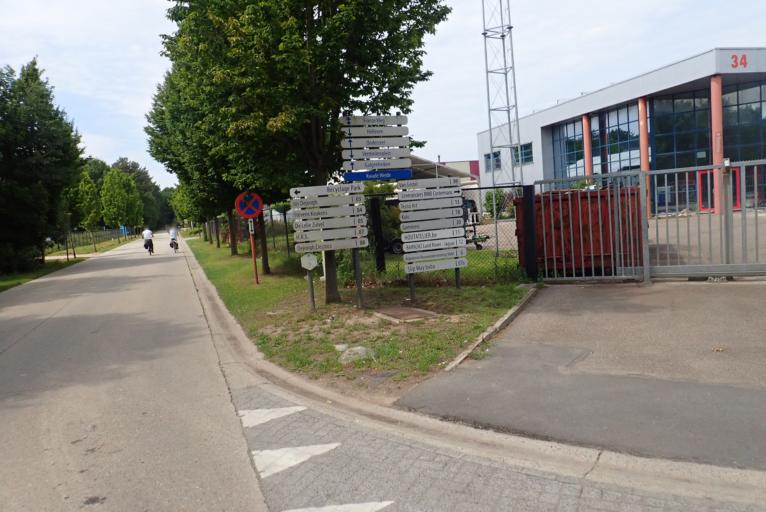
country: BE
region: Flanders
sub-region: Provincie Antwerpen
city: Kalmthout
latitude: 51.3645
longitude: 4.5019
